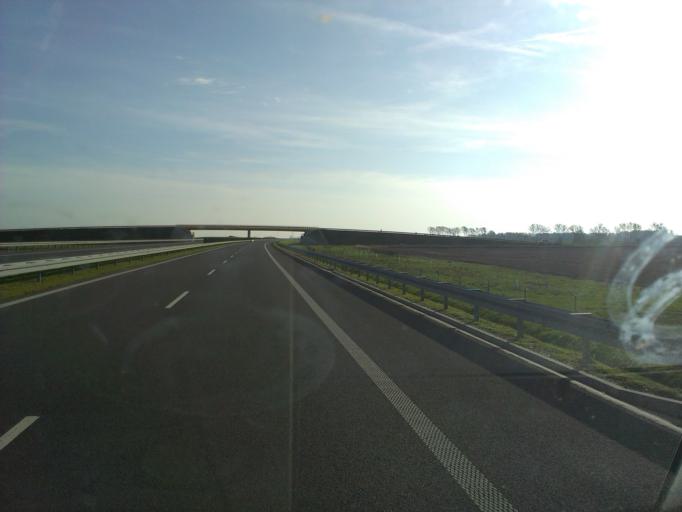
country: PL
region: West Pomeranian Voivodeship
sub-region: Powiat pyrzycki
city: Kozielice
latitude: 53.0880
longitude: 14.8393
